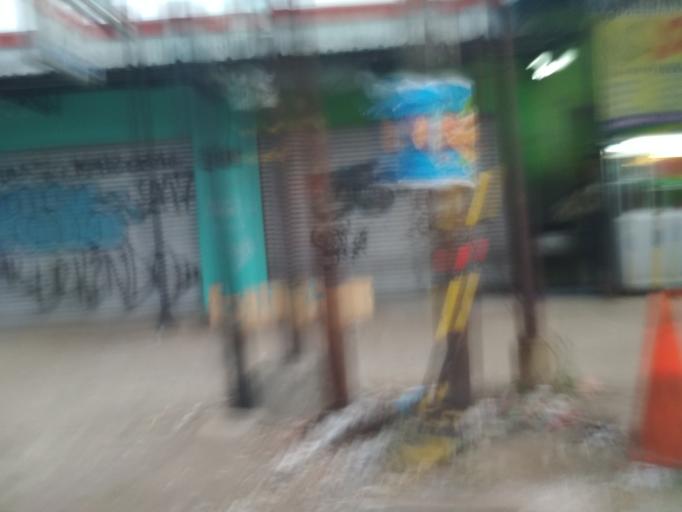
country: ID
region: West Java
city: Caringin
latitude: -6.7033
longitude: 106.8253
